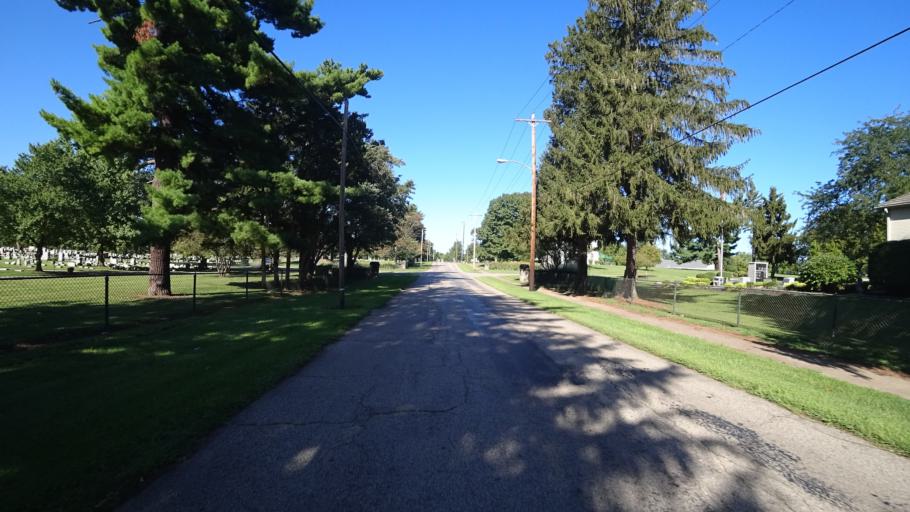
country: US
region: Ohio
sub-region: Butler County
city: Hamilton
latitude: 39.4056
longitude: -84.5391
